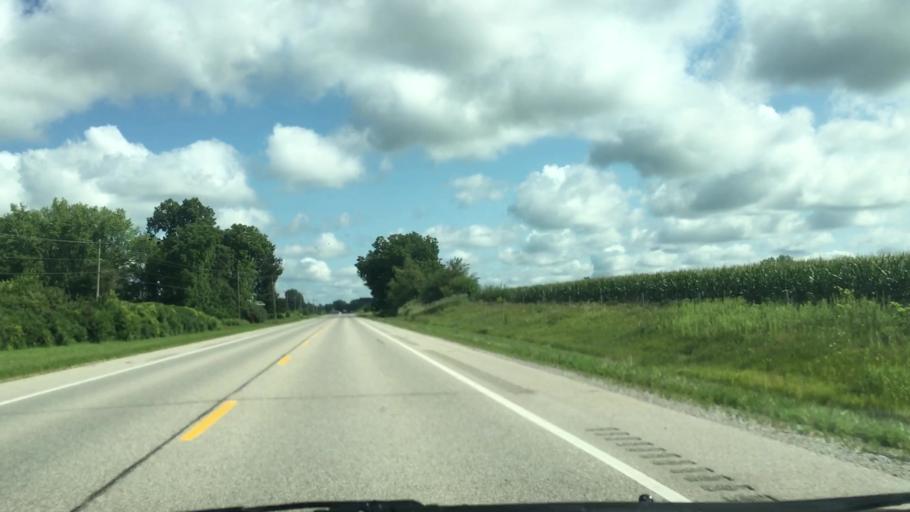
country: US
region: Iowa
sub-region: Johnson County
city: Solon
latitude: 41.7264
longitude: -91.4772
